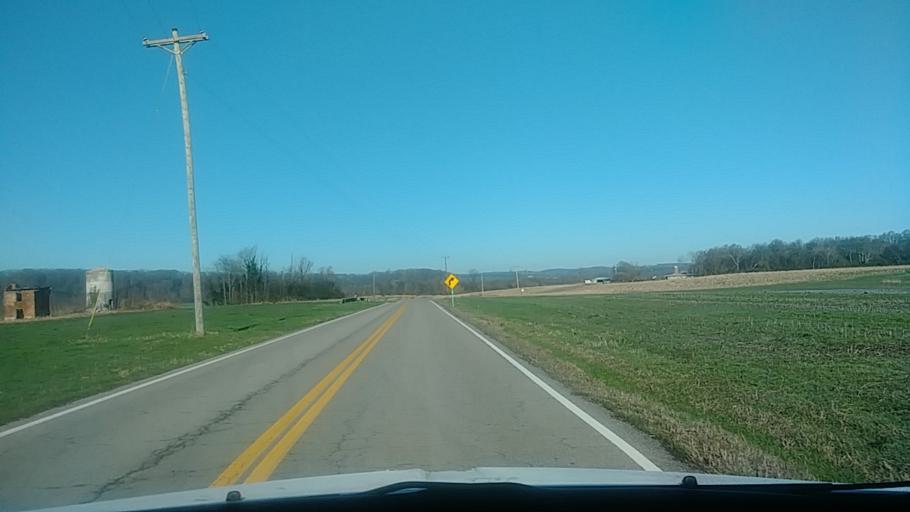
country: US
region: Tennessee
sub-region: Jefferson County
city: White Pine
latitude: 36.1520
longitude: -83.1570
